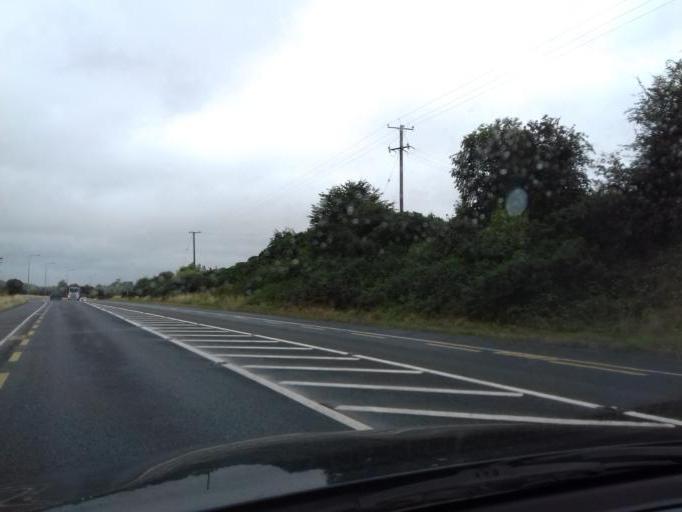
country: IE
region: Leinster
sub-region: County Carlow
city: Bagenalstown
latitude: 52.7629
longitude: -6.9561
